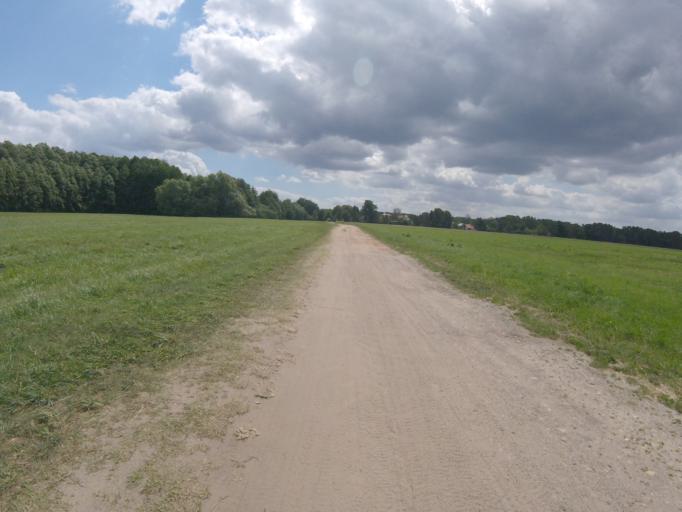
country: DE
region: Brandenburg
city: Bestensee
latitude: 52.2383
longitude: 13.6181
